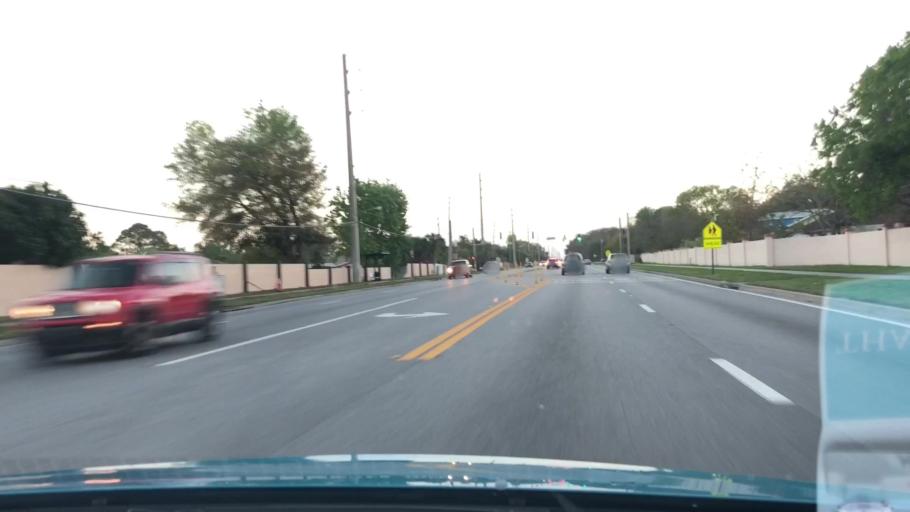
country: US
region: Florida
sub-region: Osceola County
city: Kissimmee
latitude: 28.3167
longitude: -81.3913
